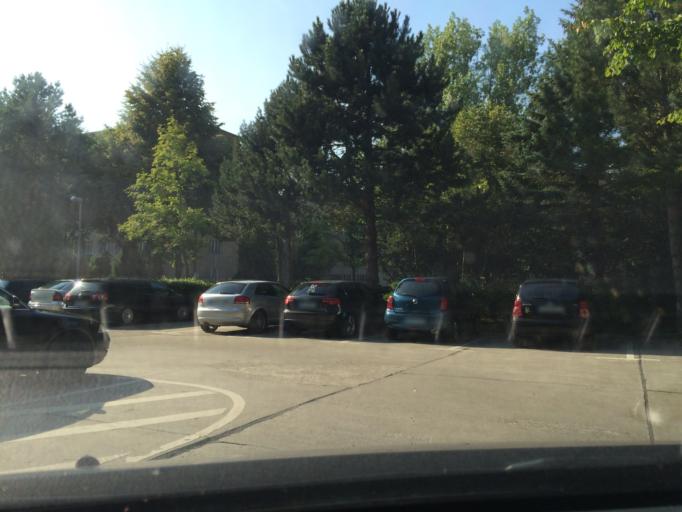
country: DE
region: Mecklenburg-Vorpommern
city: Ostseebad Binz
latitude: 54.4383
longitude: 13.5751
